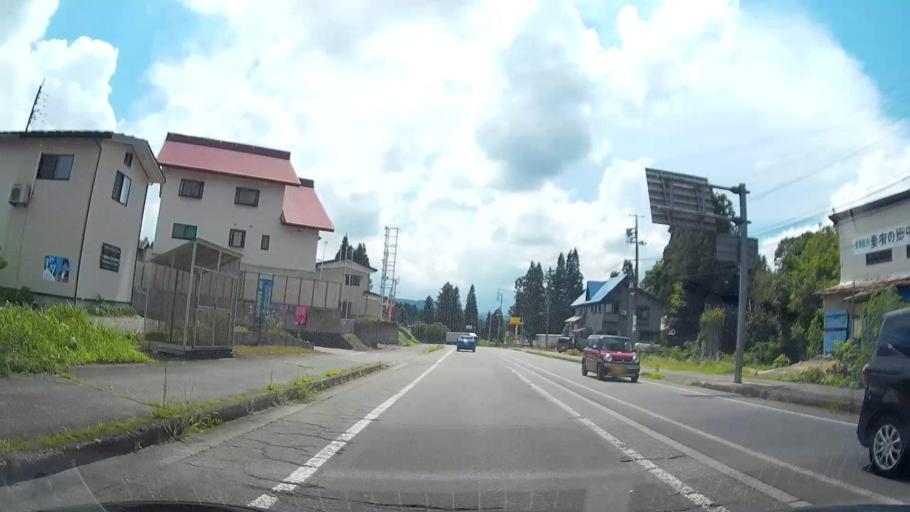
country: JP
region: Niigata
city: Tokamachi
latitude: 37.0294
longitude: 138.6658
